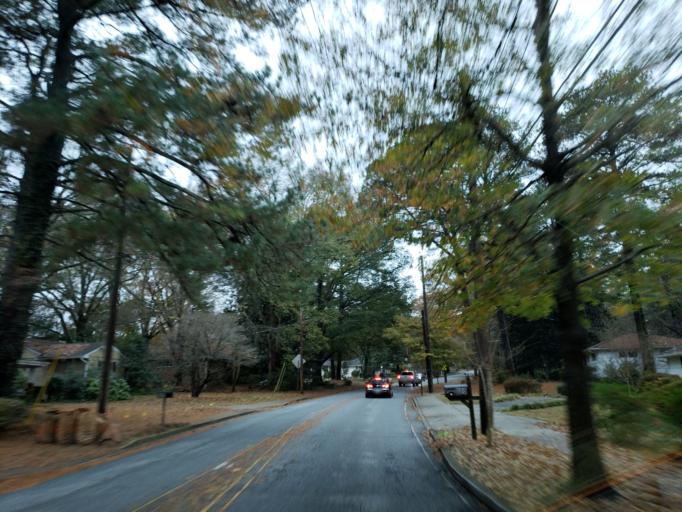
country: US
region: Georgia
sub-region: DeKalb County
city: Druid Hills
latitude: 33.8213
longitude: -84.3747
